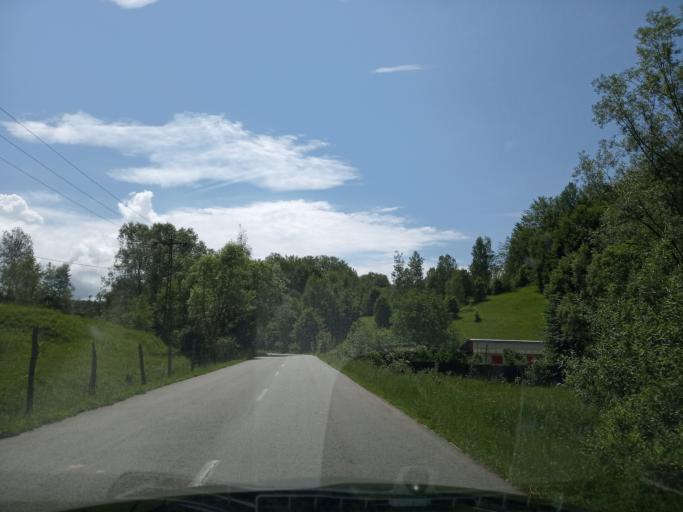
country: RO
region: Hunedoara
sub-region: Oras Petrila
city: Petrila
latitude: 45.4062
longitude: 23.4119
